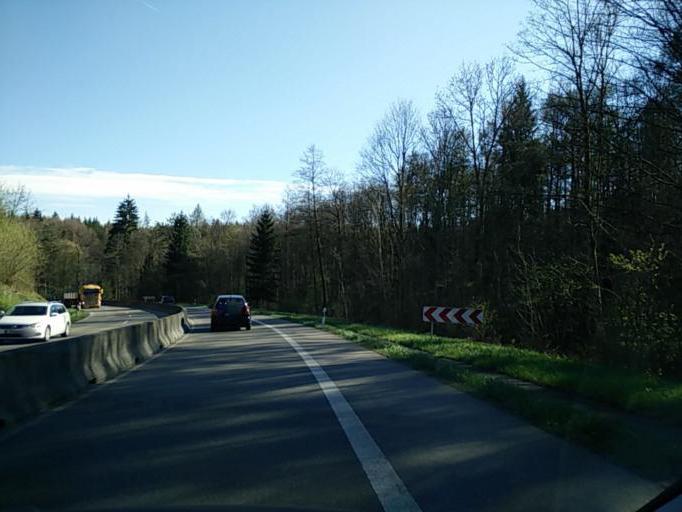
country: DE
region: Baden-Wuerttemberg
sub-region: Regierungsbezirk Stuttgart
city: Weil im Schonbuch
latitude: 48.5818
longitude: 9.0659
